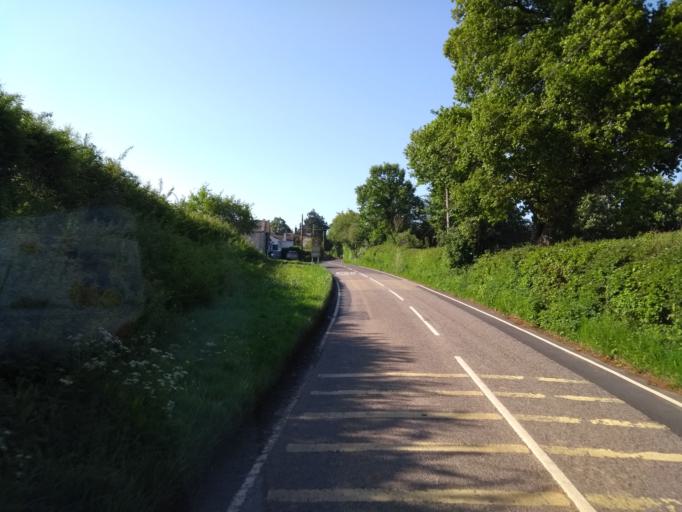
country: GB
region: England
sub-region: Somerset
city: Taunton
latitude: 50.9736
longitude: -3.0950
